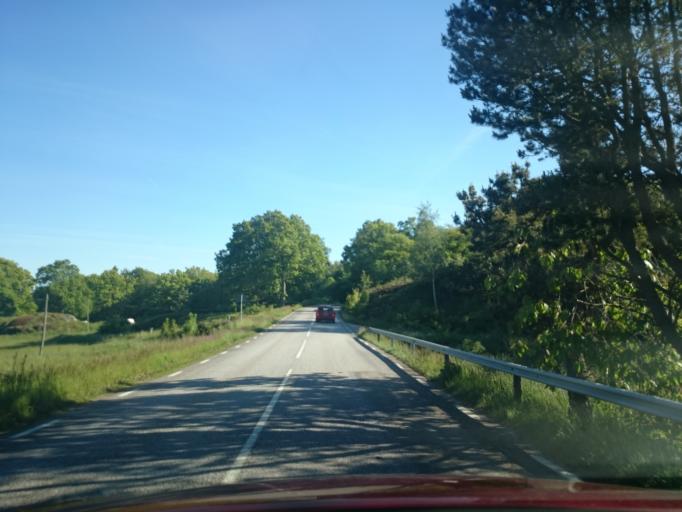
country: SE
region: Vaestra Goetaland
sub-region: Lysekils Kommun
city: Lysekil
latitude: 58.2527
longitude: 11.4899
